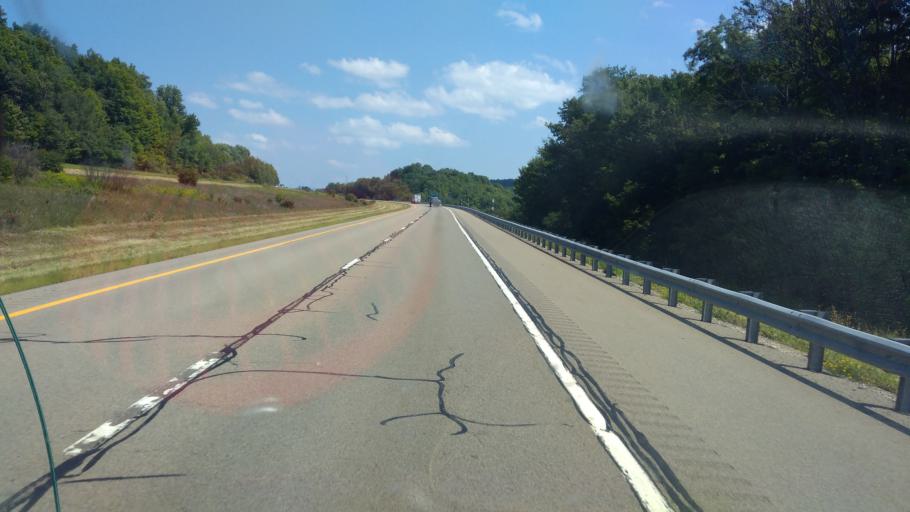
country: US
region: New York
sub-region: Steuben County
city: Hornell
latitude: 42.3734
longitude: -77.5636
